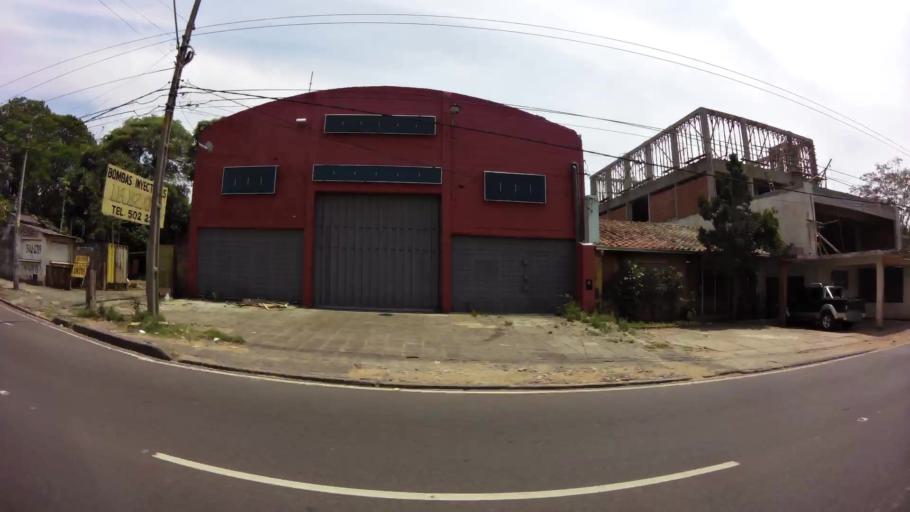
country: PY
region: Central
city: Fernando de la Mora
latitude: -25.3171
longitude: -57.5582
